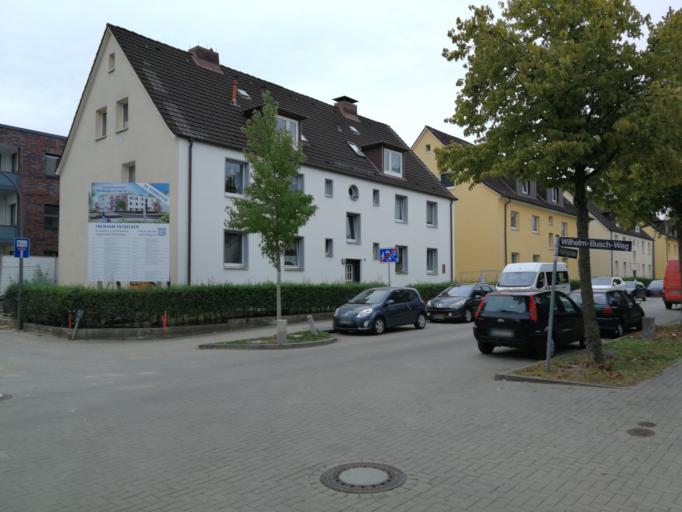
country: DE
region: Hamburg
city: Harburg
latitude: 53.4595
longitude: 9.9618
